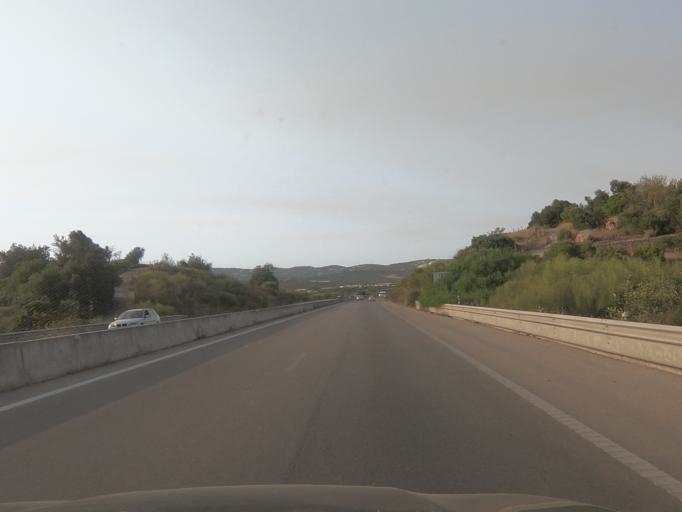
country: PT
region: Faro
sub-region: Loule
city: Almancil
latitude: 37.1099
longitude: -8.0454
